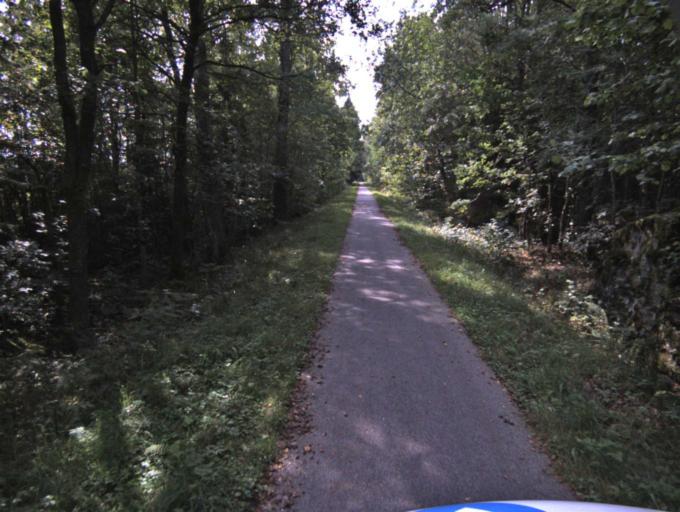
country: SE
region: Vaestra Goetaland
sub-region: Tranemo Kommun
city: Limmared
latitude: 57.6280
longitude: 13.3489
